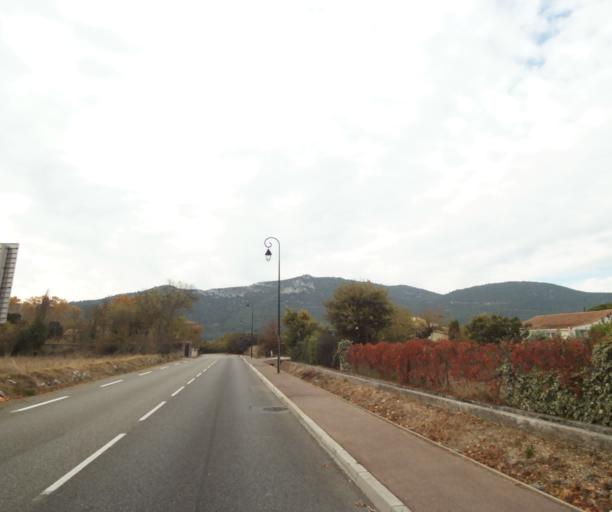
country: FR
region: Provence-Alpes-Cote d'Azur
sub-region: Departement des Bouches-du-Rhone
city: Gemenos
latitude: 43.2882
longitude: 5.6248
